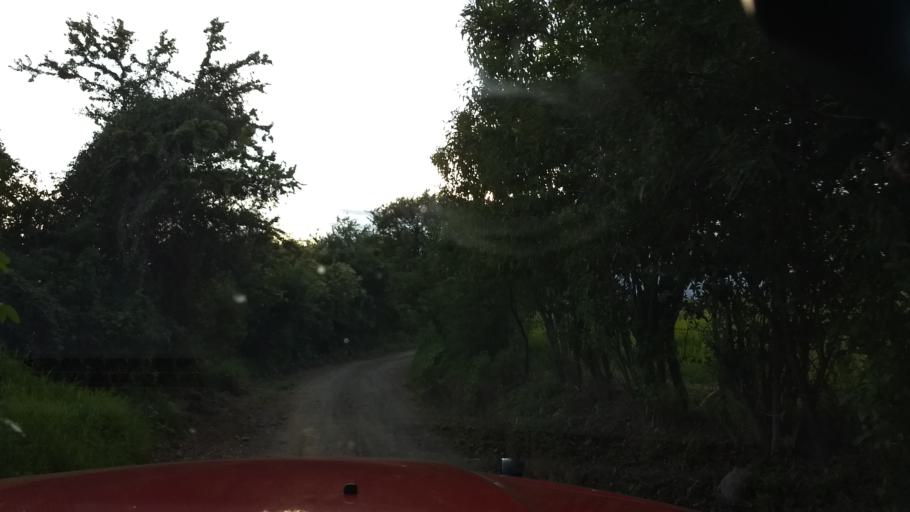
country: MX
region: Colima
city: Suchitlan
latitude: 19.4967
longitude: -103.7720
